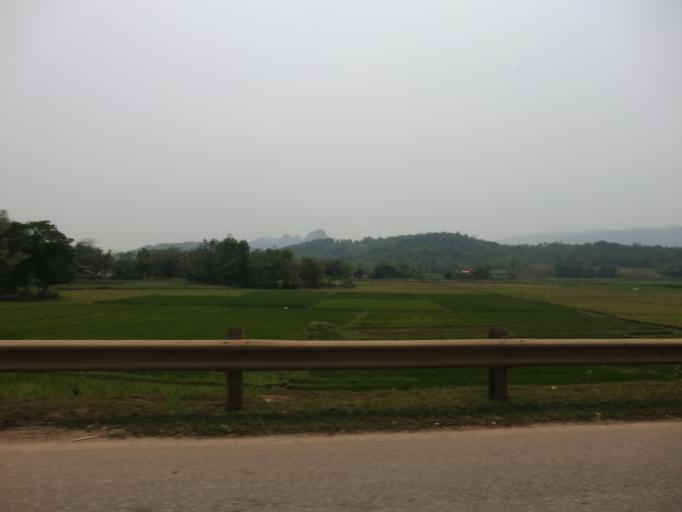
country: VN
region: Thanh Hoa
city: Thi Tran Ngoc Lac
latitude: 20.1055
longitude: 105.3783
